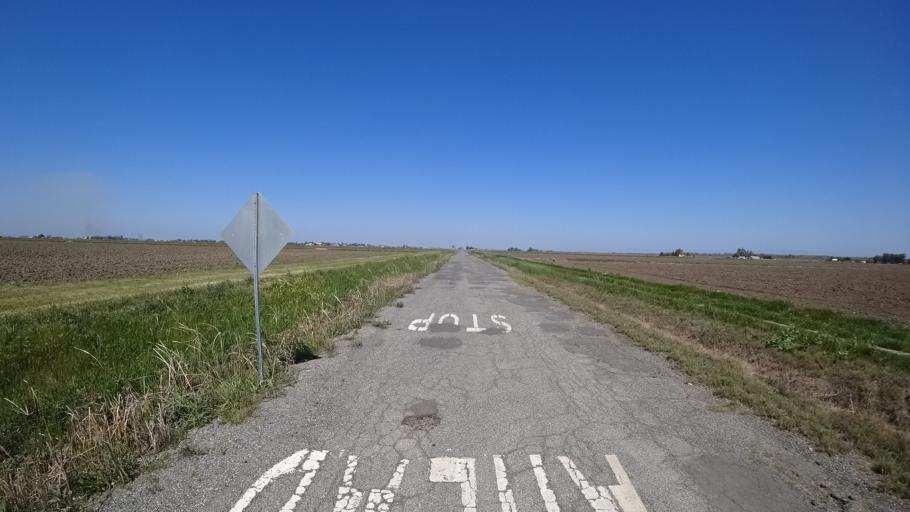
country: US
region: California
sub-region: Glenn County
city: Willows
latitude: 39.5595
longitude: -122.0277
